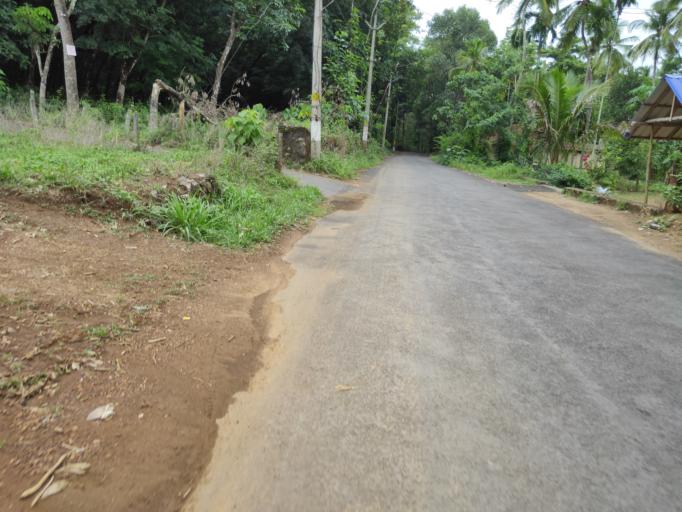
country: IN
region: Kerala
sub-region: Malappuram
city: Manjeri
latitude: 11.2410
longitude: 76.2464
